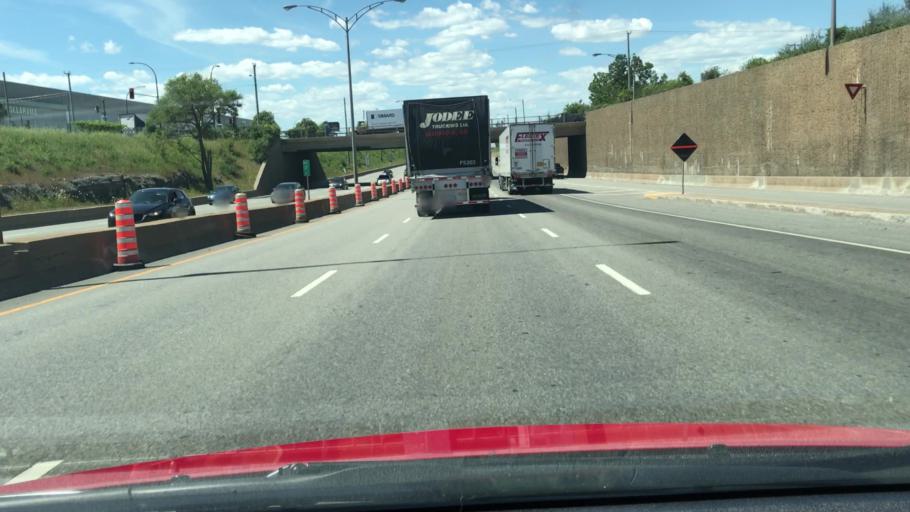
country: CA
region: Quebec
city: Cote-Saint-Luc
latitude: 45.4671
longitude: -73.6978
